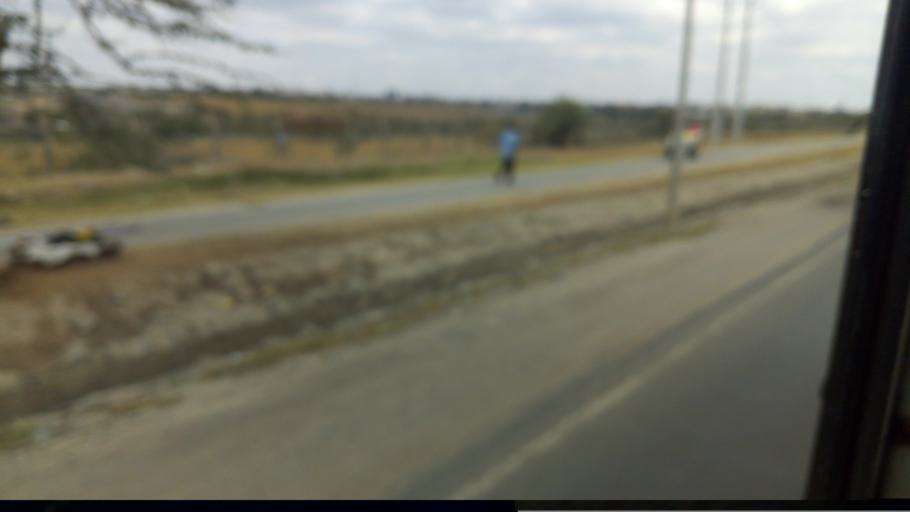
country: KE
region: Machakos
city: Athi River
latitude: -1.4600
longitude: 36.9646
